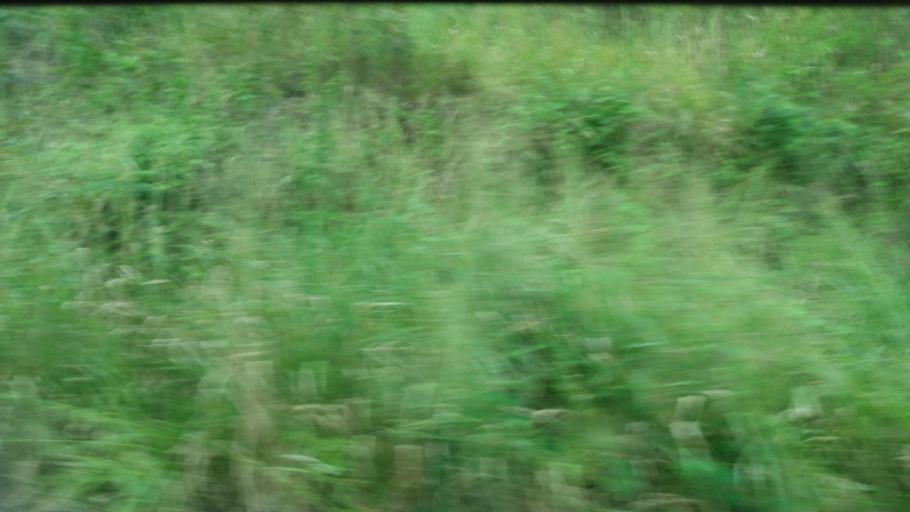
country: BR
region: Pernambuco
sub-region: Maraial
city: Maraial
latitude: -8.7176
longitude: -35.7810
